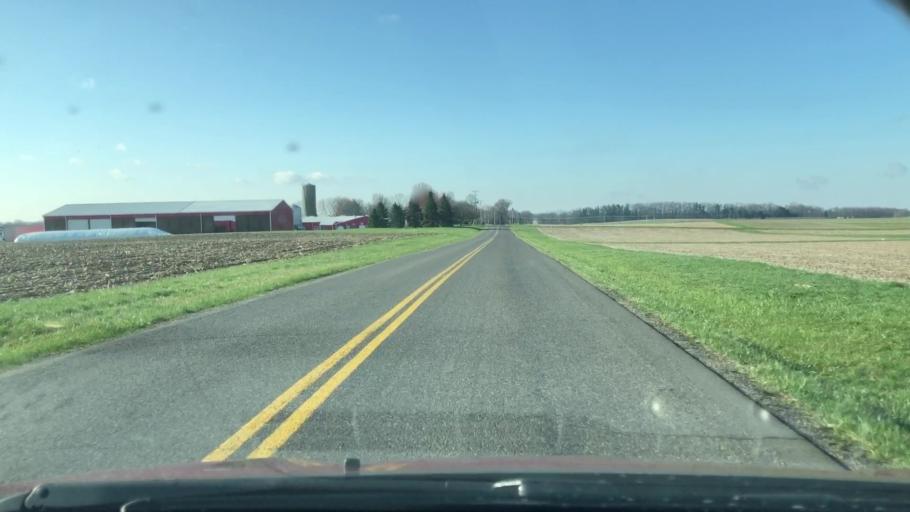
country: US
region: Ohio
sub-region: Wayne County
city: Wooster
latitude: 40.7748
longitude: -81.9058
